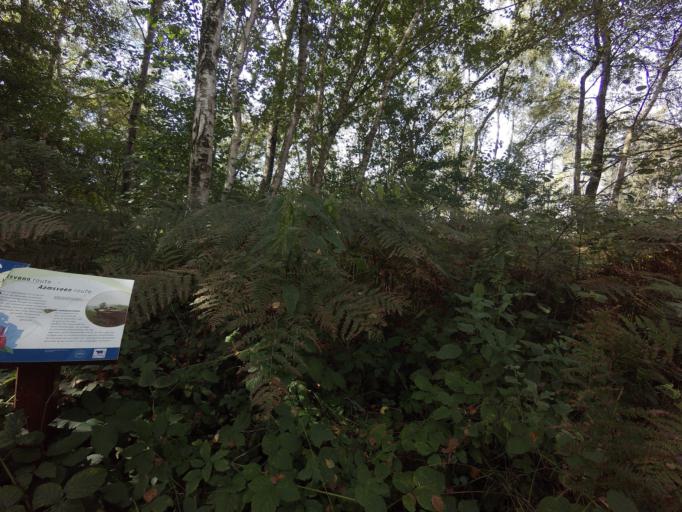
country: DE
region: North Rhine-Westphalia
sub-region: Regierungsbezirk Munster
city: Gronau
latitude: 52.1819
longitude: 6.9603
